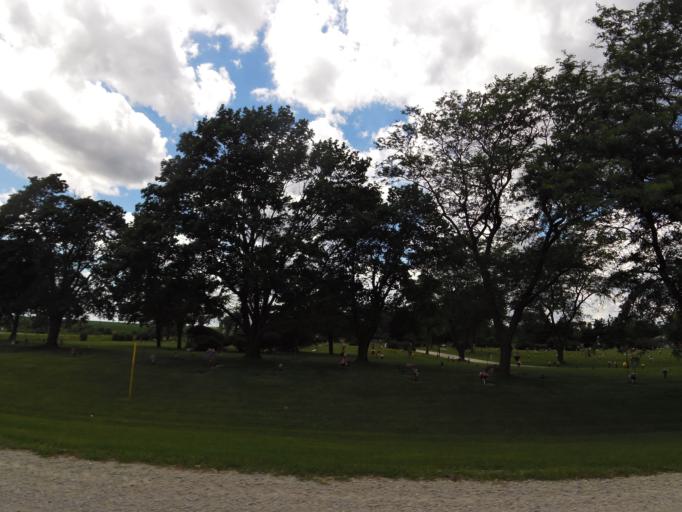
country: US
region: Iowa
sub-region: Fayette County
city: Oelwein
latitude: 42.6289
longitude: -91.9091
